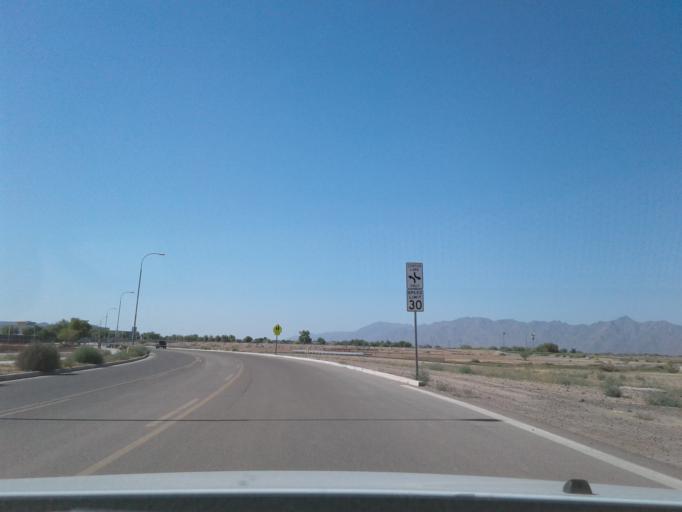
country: US
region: Arizona
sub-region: Maricopa County
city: Laveen
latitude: 33.3763
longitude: -112.1851
